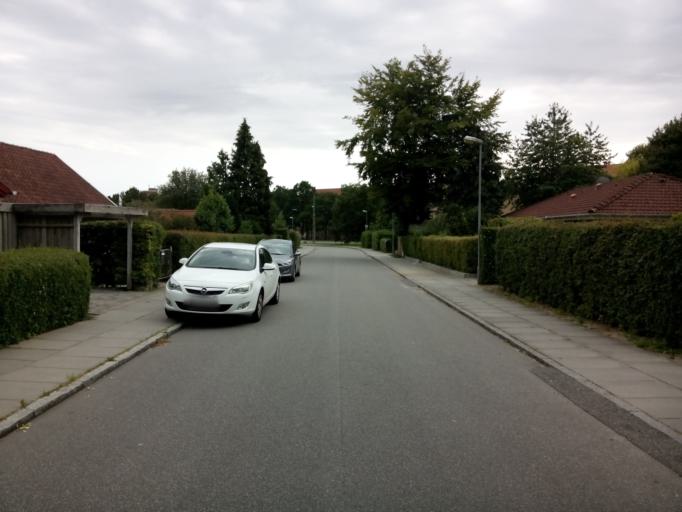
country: DK
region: Central Jutland
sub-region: Arhus Kommune
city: Arhus
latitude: 56.1761
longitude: 10.1818
